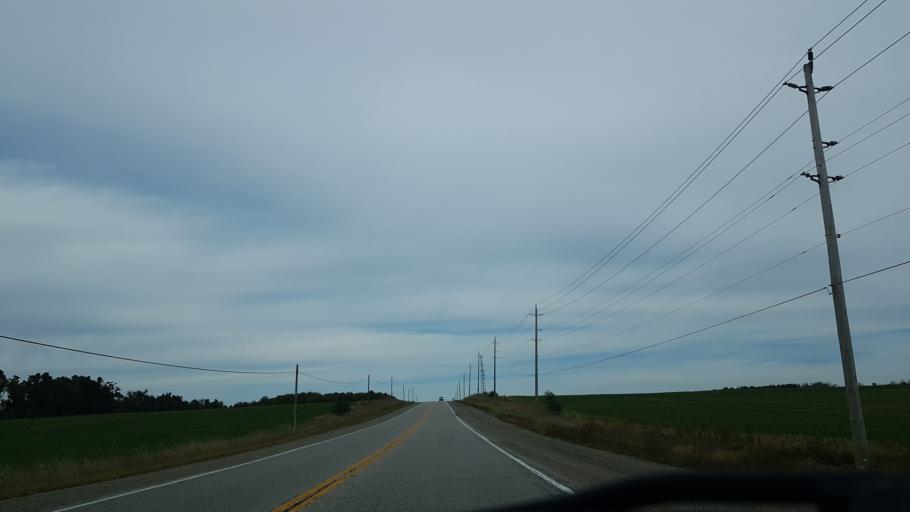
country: CA
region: Ontario
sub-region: Wellington County
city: Guelph
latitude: 43.6705
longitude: -80.1637
